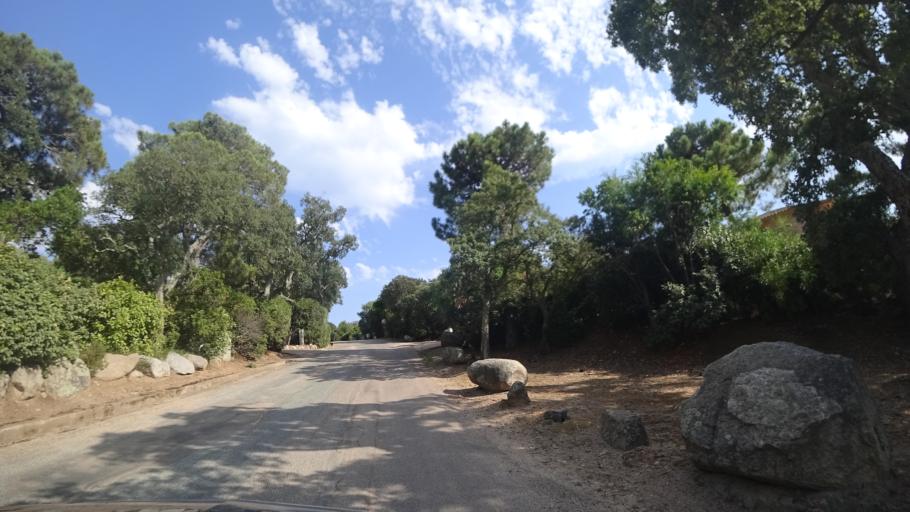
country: FR
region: Corsica
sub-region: Departement de la Corse-du-Sud
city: Porto-Vecchio
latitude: 41.6205
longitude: 9.3457
